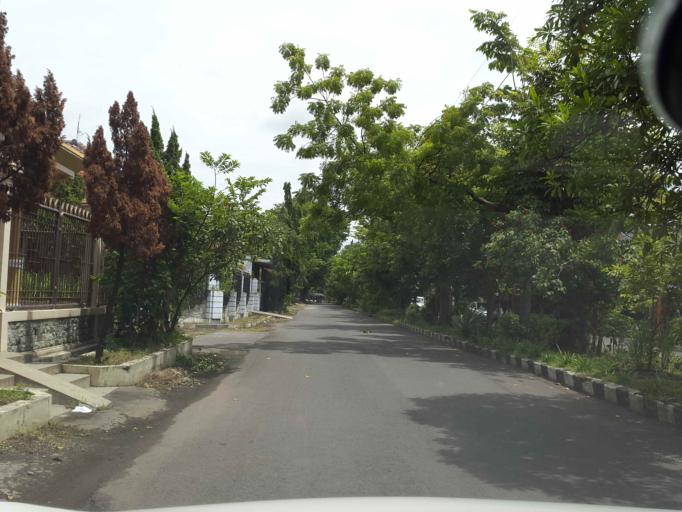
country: ID
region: East Java
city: Mojokerto
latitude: -7.4628
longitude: 112.4443
